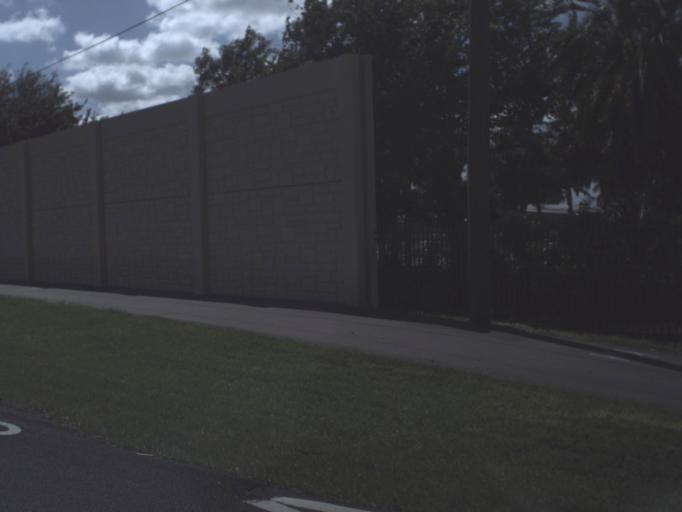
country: US
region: Florida
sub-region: Collier County
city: Lely Resort
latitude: 26.0432
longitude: -81.6682
